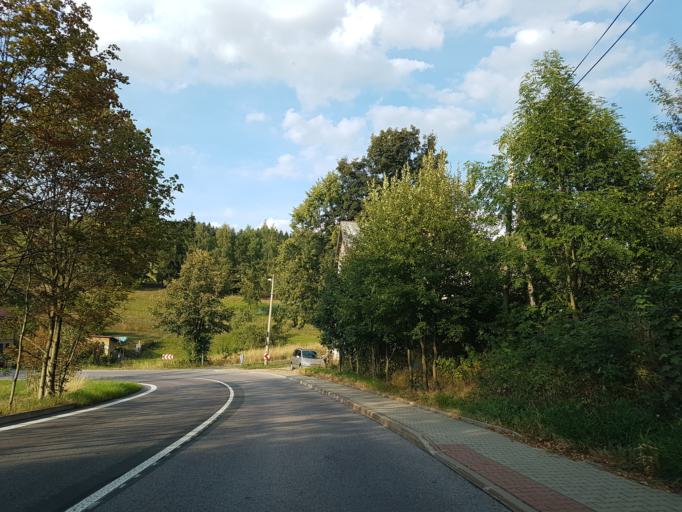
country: CZ
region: Liberecky
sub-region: Okres Jablonec nad Nisou
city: Jablonec nad Nisou
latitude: 50.6987
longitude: 15.1913
